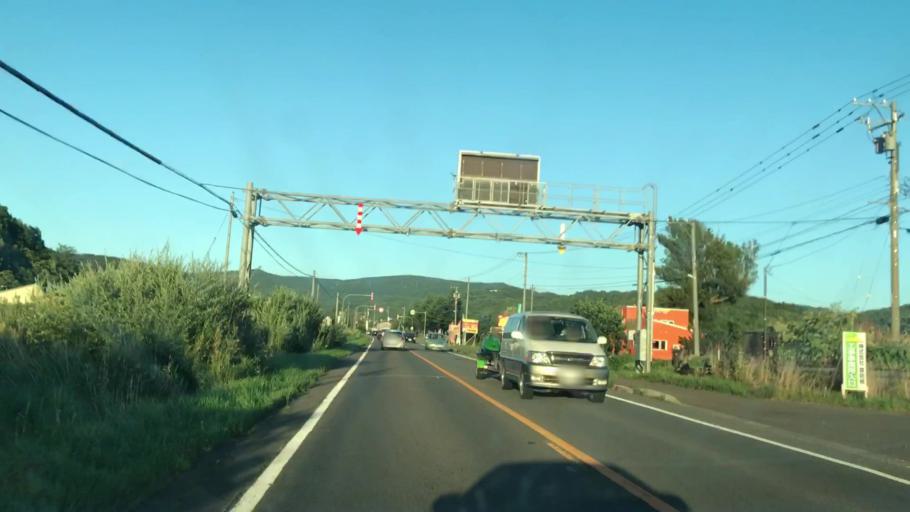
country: JP
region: Hokkaido
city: Niseko Town
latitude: 42.7974
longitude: 140.9528
